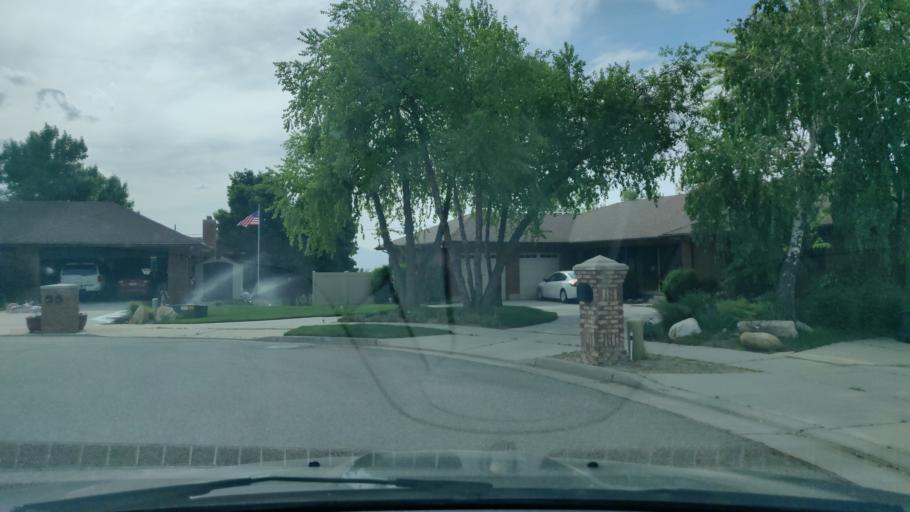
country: US
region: Utah
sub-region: Salt Lake County
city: Cottonwood Heights
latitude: 40.6179
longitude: -111.8074
